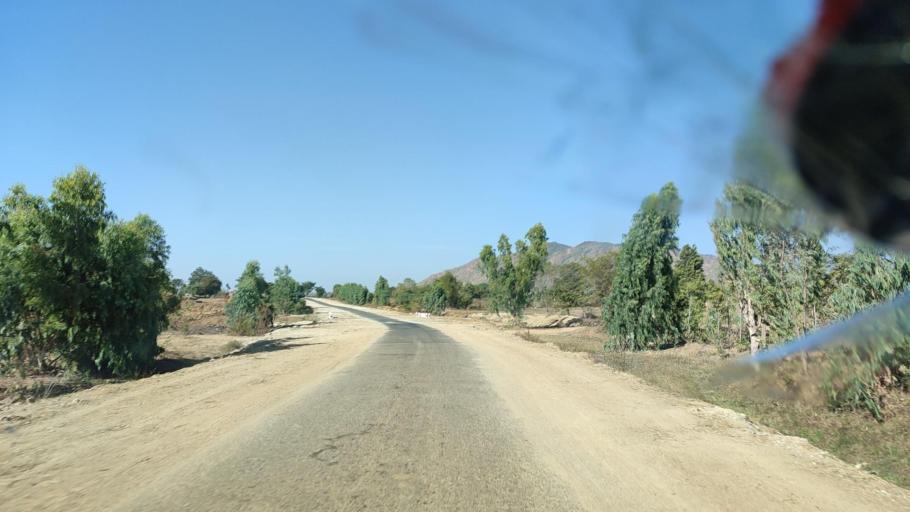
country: MM
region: Mandalay
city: Yamethin
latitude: 20.2389
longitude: 96.2617
